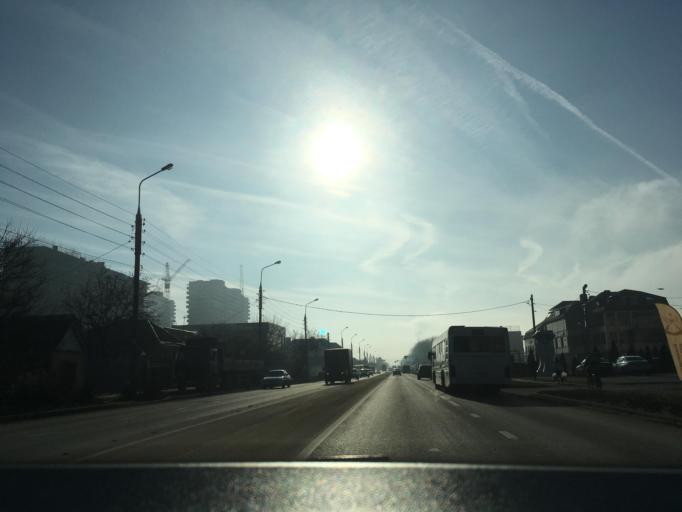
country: RU
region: Krasnodarskiy
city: Krasnodar
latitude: 45.1091
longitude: 39.0124
